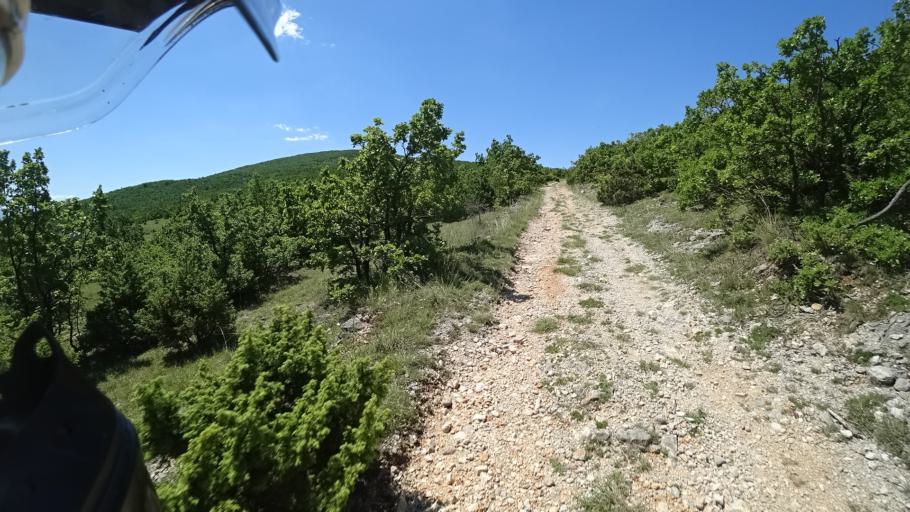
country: HR
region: Sibensko-Kniniska
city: Knin
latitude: 44.0132
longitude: 16.3398
